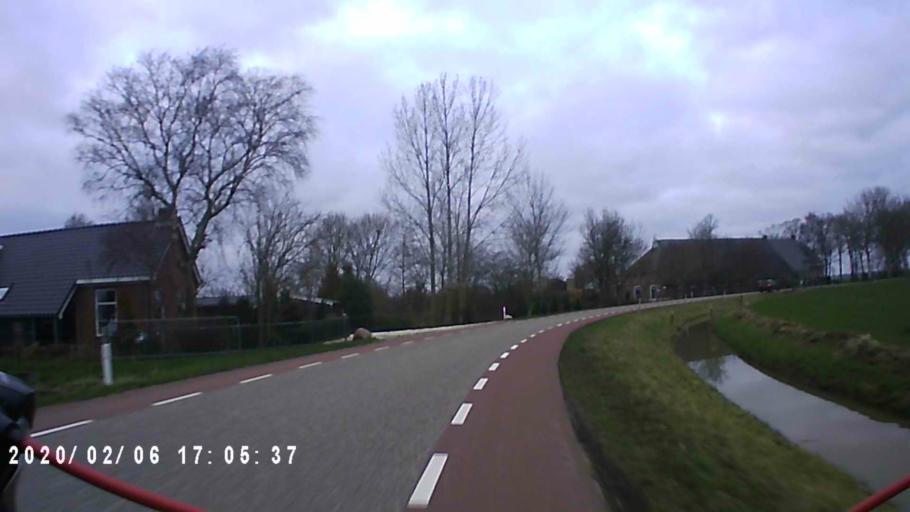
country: NL
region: Groningen
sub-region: Gemeente Zuidhorn
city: Aduard
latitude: 53.2732
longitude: 6.5102
